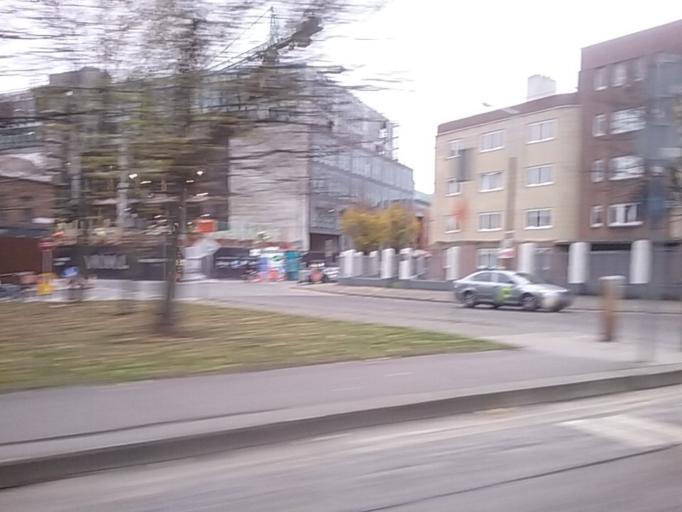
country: IE
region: Leinster
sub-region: Dublin City
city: Dublin
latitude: 53.3450
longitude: -6.2473
